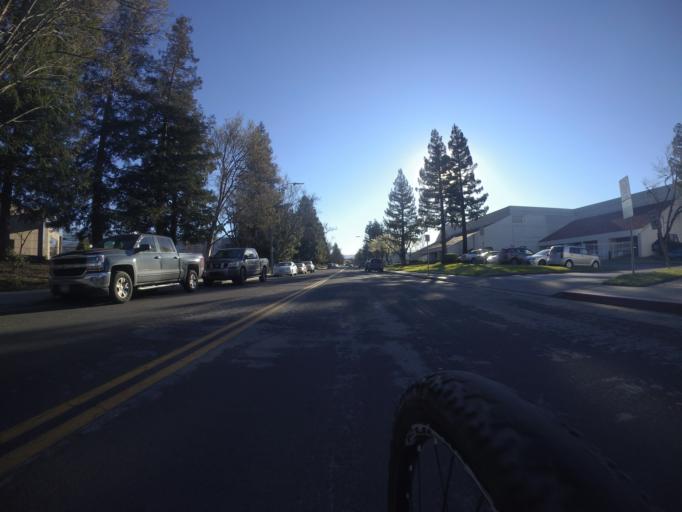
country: US
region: California
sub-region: Santa Clara County
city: Milpitas
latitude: 37.4143
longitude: -121.9475
